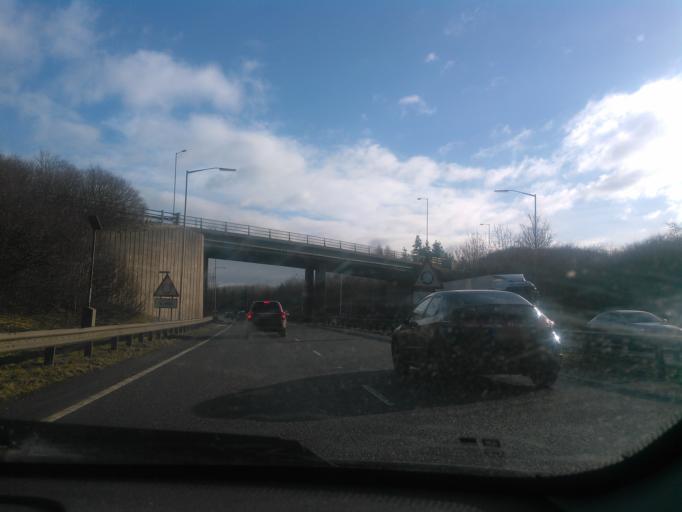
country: GB
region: England
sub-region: Staffordshire
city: Uttoxeter
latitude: 52.9110
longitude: -1.8895
